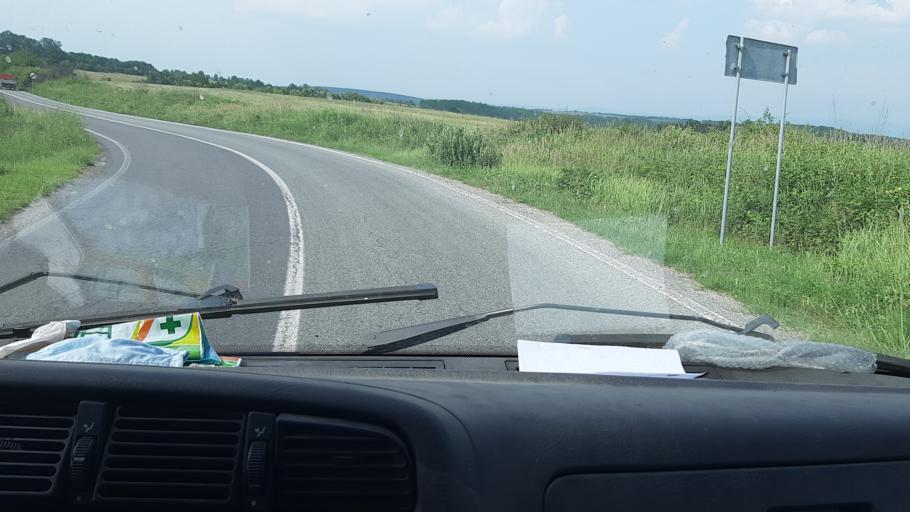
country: RO
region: Caras-Severin
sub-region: Comuna Farliug
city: Farliug
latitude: 45.5252
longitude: 21.8784
